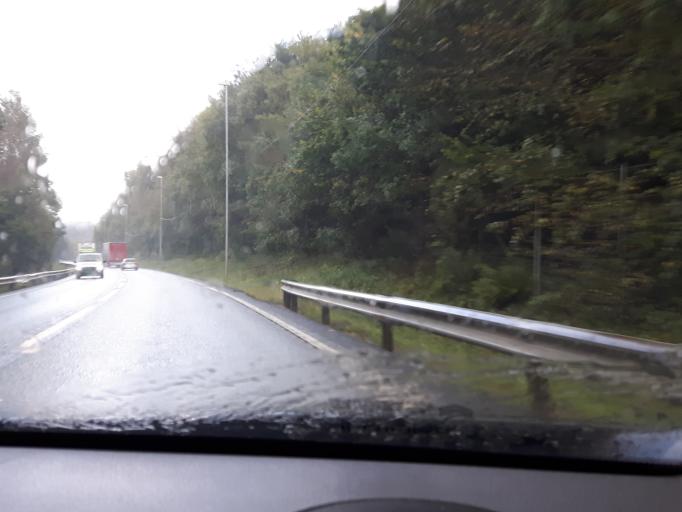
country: NO
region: Vest-Agder
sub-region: Sogne
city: Sogne
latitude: 58.0958
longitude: 7.7238
